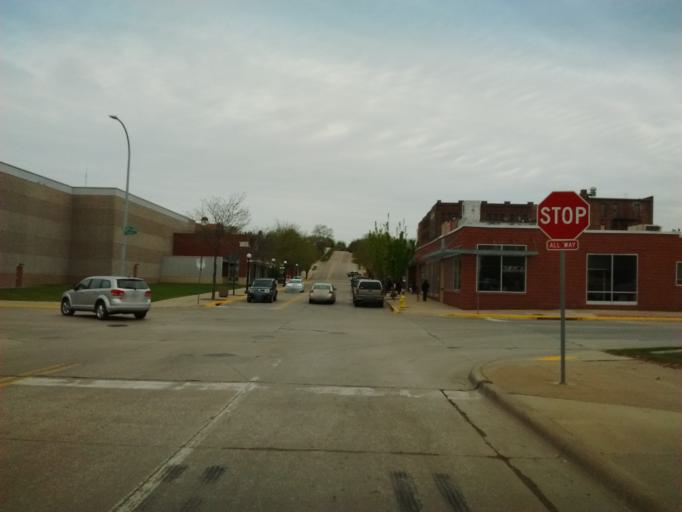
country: US
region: Iowa
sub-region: Woodbury County
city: Sioux City
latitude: 42.4929
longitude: -96.3977
